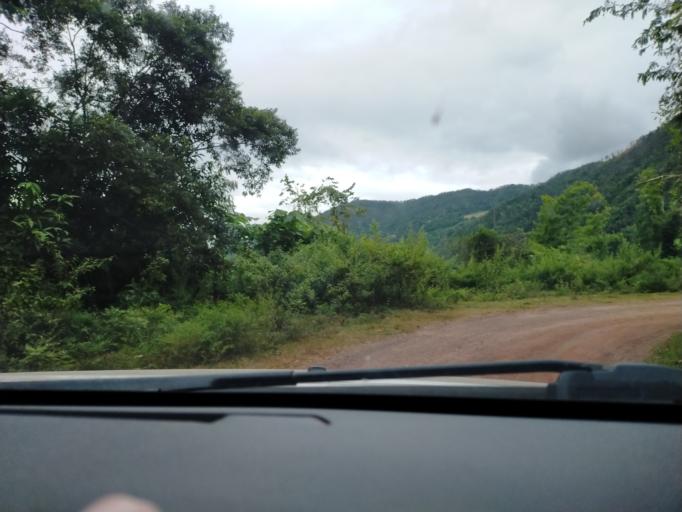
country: TH
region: Nan
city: Chaloem Phra Kiat
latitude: 19.7752
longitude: 101.3488
